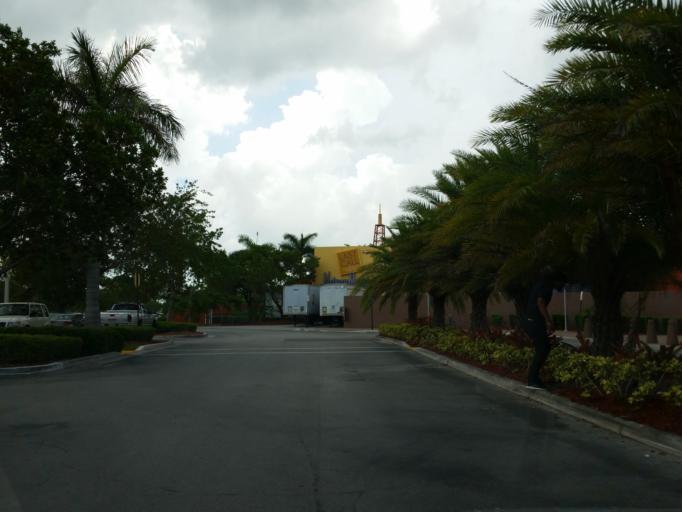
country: US
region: Florida
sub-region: Miami-Dade County
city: Sweetwater
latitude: 25.7890
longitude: -80.3816
